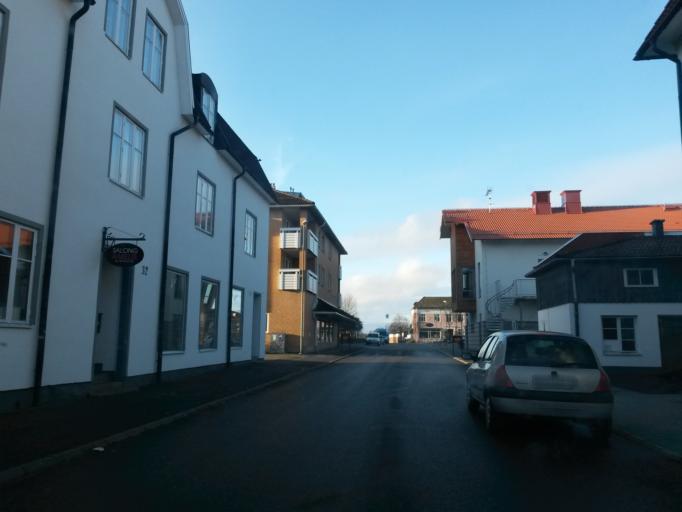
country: SE
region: Vaestra Goetaland
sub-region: Grastorps Kommun
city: Graestorp
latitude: 58.3343
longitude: 12.6834
